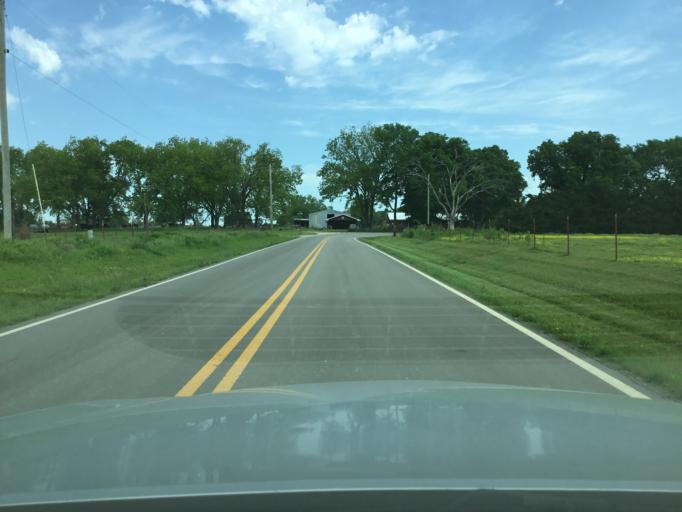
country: US
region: Kansas
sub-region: Montgomery County
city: Coffeyville
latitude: 37.0069
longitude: -95.5904
